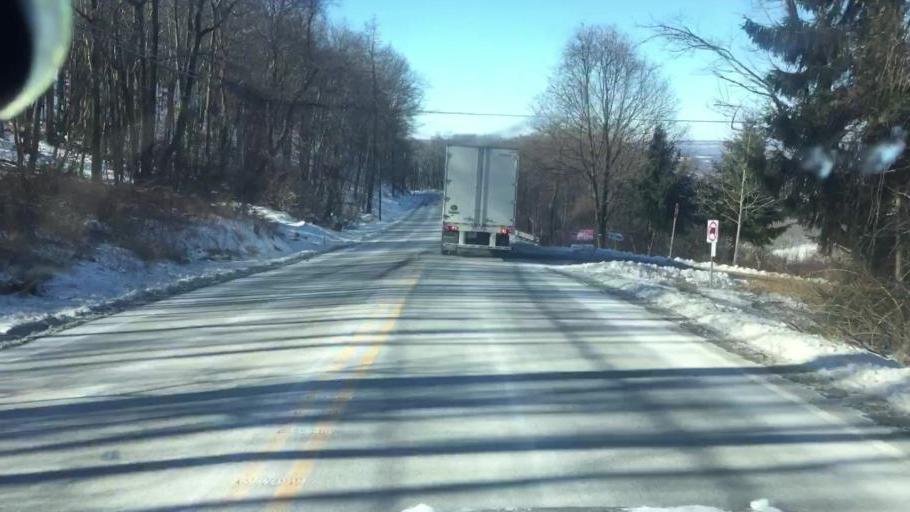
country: US
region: Pennsylvania
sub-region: Luzerne County
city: Conyngham
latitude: 41.0333
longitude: -76.1077
